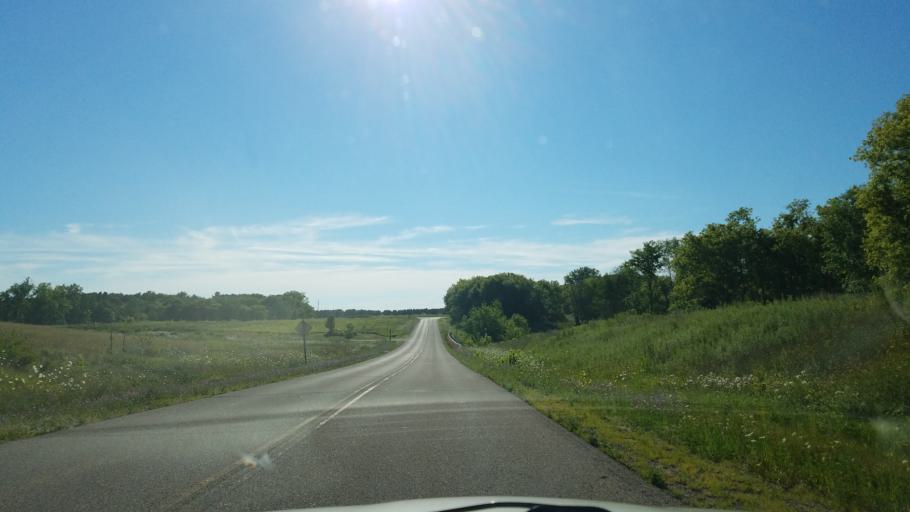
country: US
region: Wisconsin
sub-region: Saint Croix County
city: Somerset
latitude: 45.1109
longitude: -92.7225
